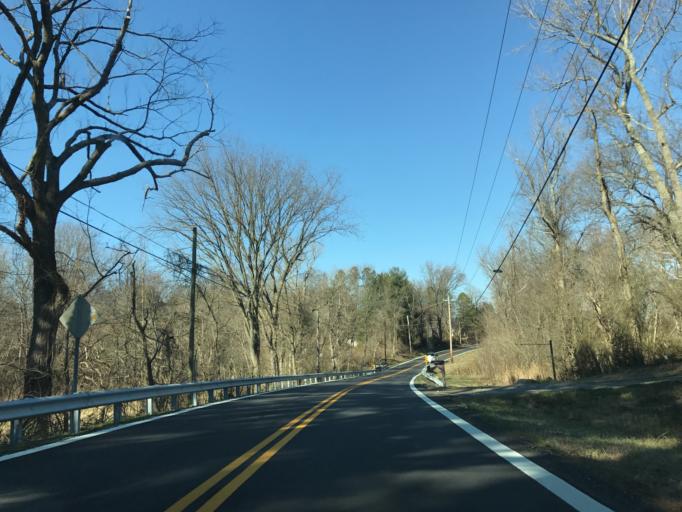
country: US
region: Maryland
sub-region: Queen Anne's County
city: Centreville
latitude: 39.0207
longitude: -76.1282
